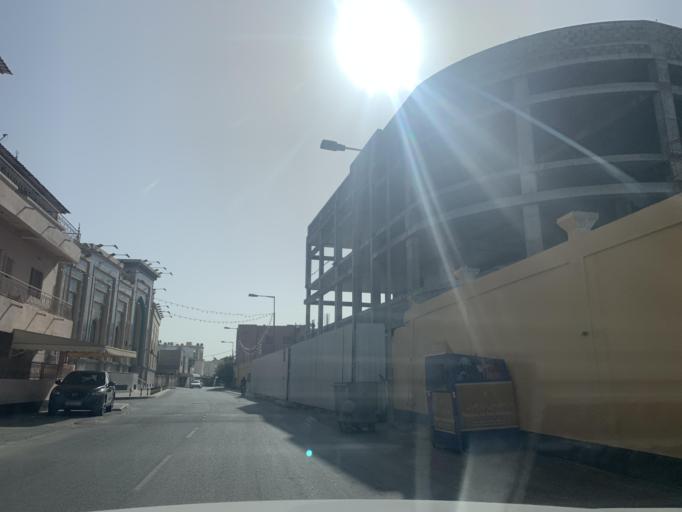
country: BH
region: Manama
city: Jidd Hafs
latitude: 26.2103
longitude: 50.5608
